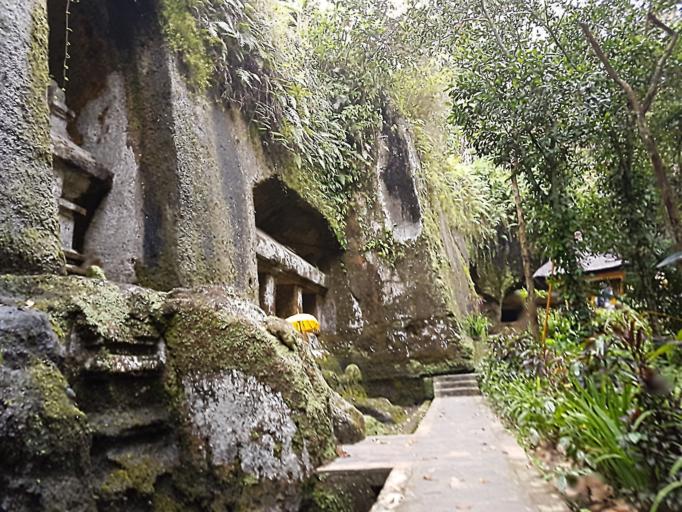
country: ID
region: Bali
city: Banjar Manukayaanyar
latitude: -8.4251
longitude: 115.3124
